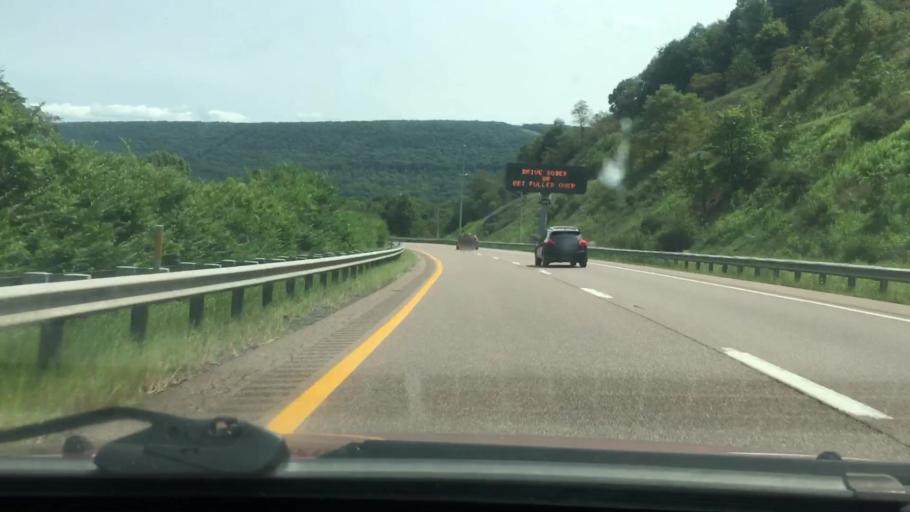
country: US
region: Maryland
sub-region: Allegany County
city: La Vale
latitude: 39.6350
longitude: -78.8457
